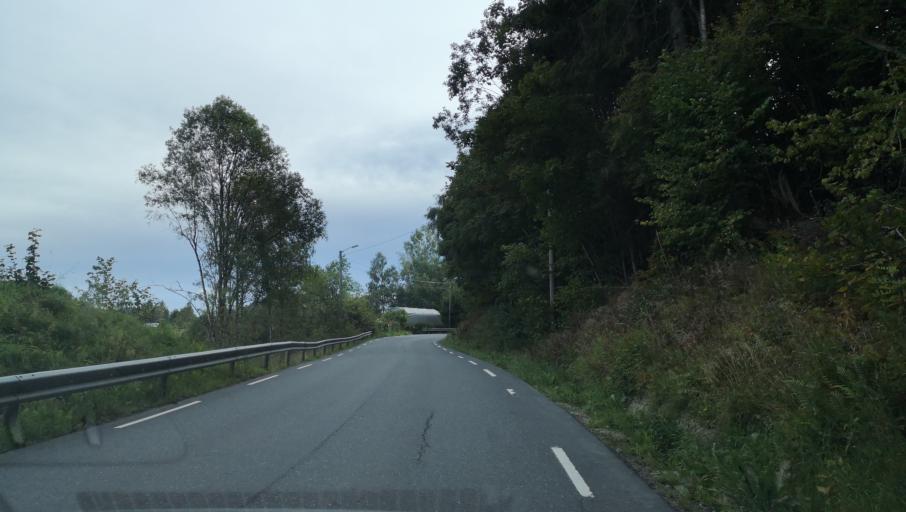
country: NO
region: Ostfold
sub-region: Hobol
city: Tomter
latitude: 59.6642
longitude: 11.0070
